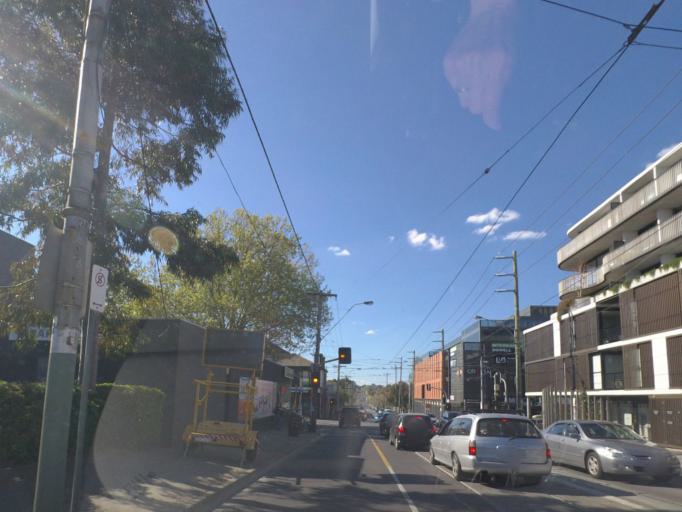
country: AU
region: Victoria
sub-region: Boroondara
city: Kew
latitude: -37.8220
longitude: 145.0263
